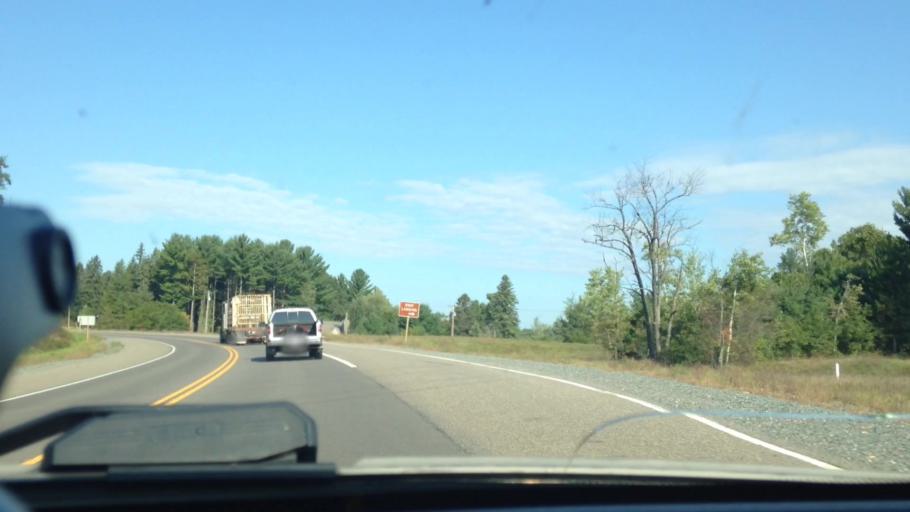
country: US
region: Michigan
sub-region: Dickinson County
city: Iron Mountain
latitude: 45.8748
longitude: -88.0858
